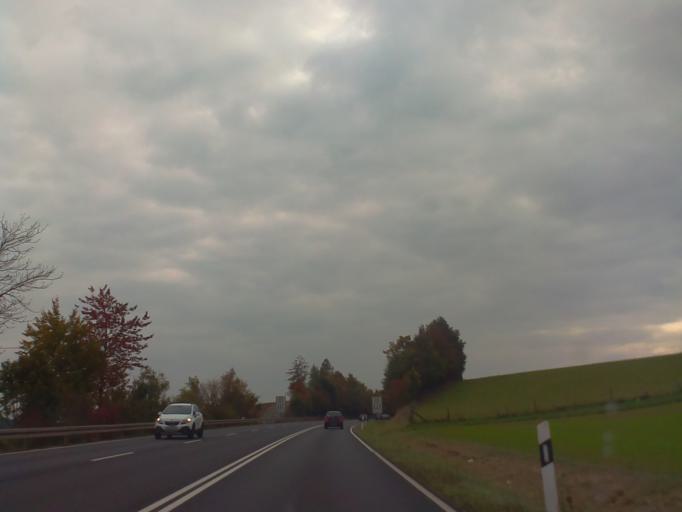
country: DE
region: Hesse
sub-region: Regierungsbezirk Kassel
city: Petersberg
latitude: 50.6159
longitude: 9.7302
